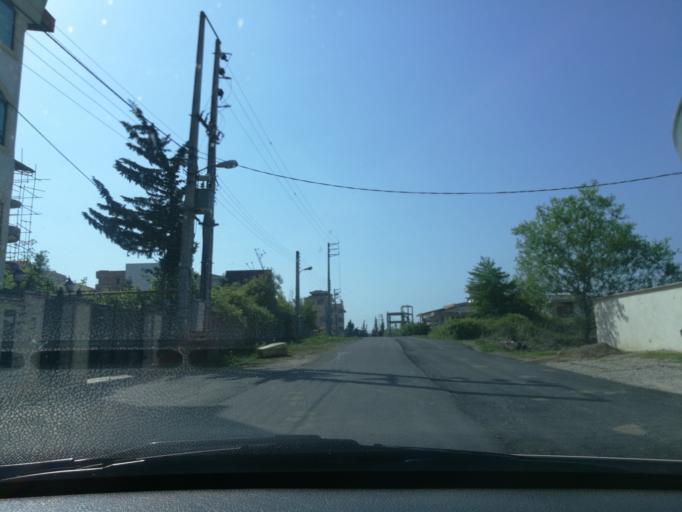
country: IR
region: Mazandaran
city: Chalus
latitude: 36.6724
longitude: 51.4321
